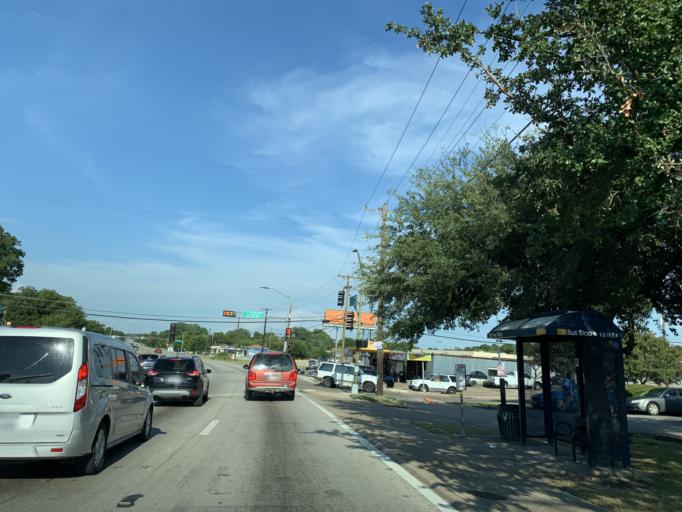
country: US
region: Texas
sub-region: Dallas County
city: Cockrell Hill
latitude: 32.6822
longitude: -96.8056
